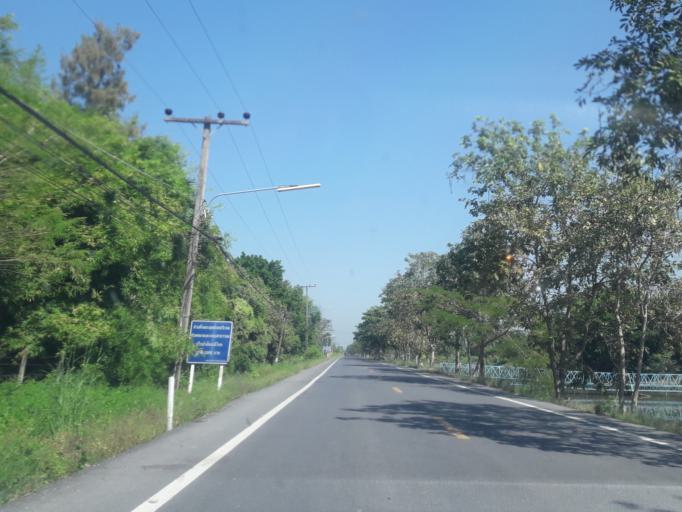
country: TH
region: Pathum Thani
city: Nong Suea
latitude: 14.1551
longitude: 100.8459
